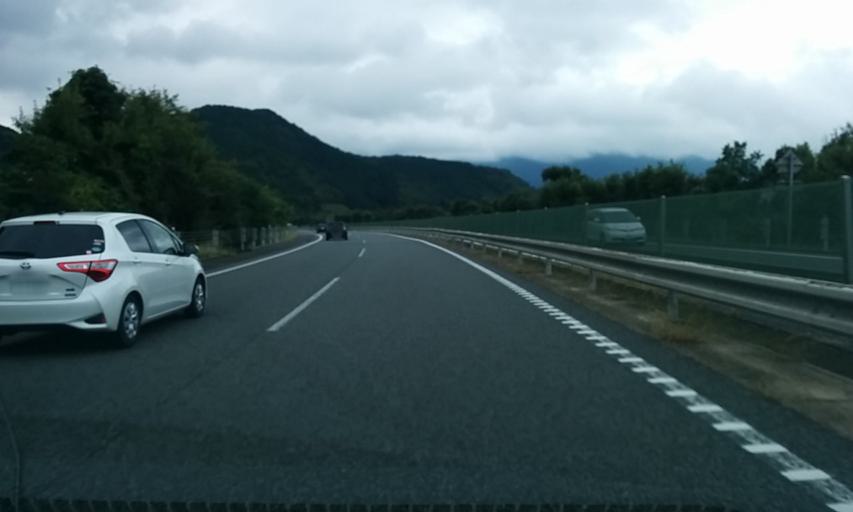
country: JP
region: Kyoto
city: Fukuchiyama
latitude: 35.1811
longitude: 135.1368
